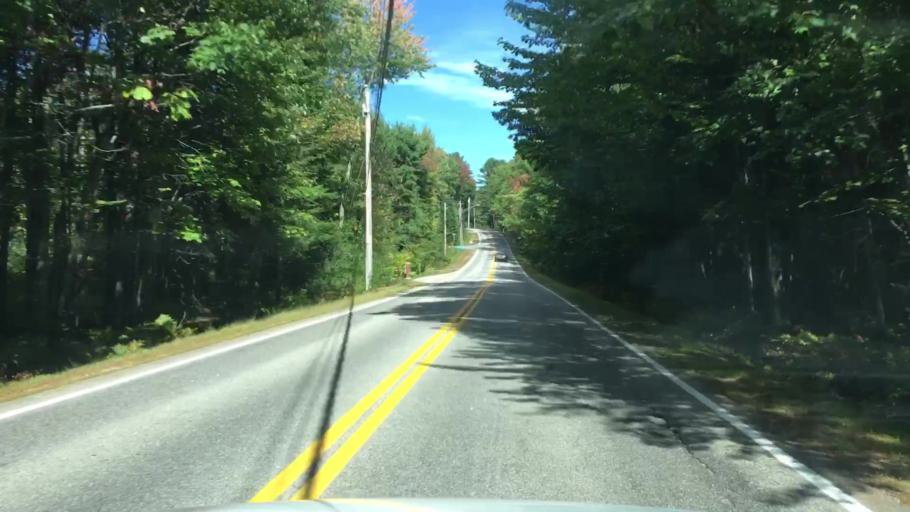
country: US
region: Maine
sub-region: Cumberland County
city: West Scarborough
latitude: 43.6000
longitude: -70.4249
